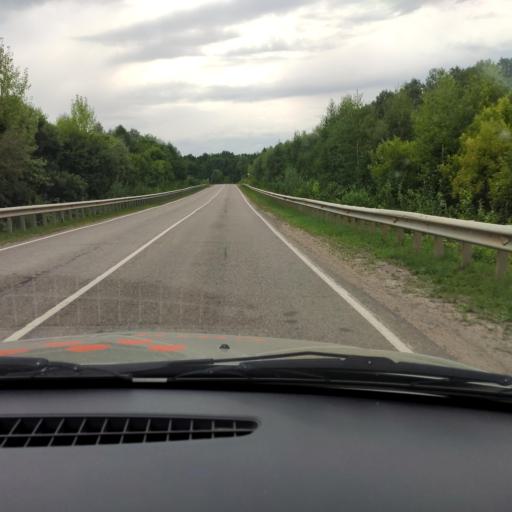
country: RU
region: Bashkortostan
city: Krasnaya Gorka
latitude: 55.2802
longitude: 56.7062
